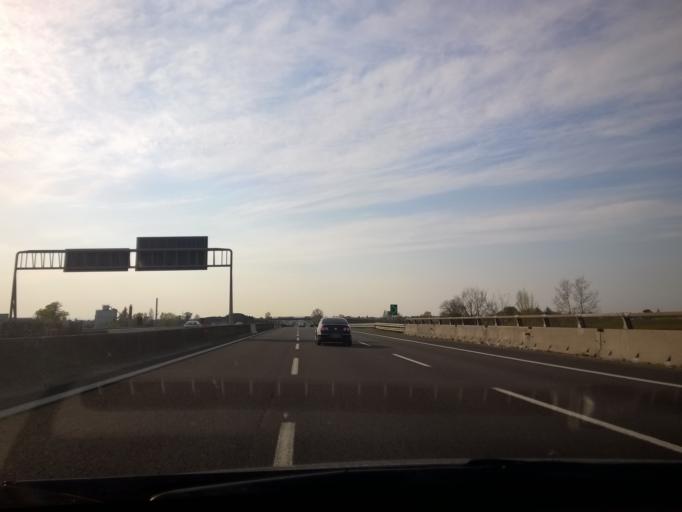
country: IT
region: Emilia-Romagna
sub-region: Forli-Cesena
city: Santa Maria Nuova
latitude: 44.1991
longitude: 12.2156
